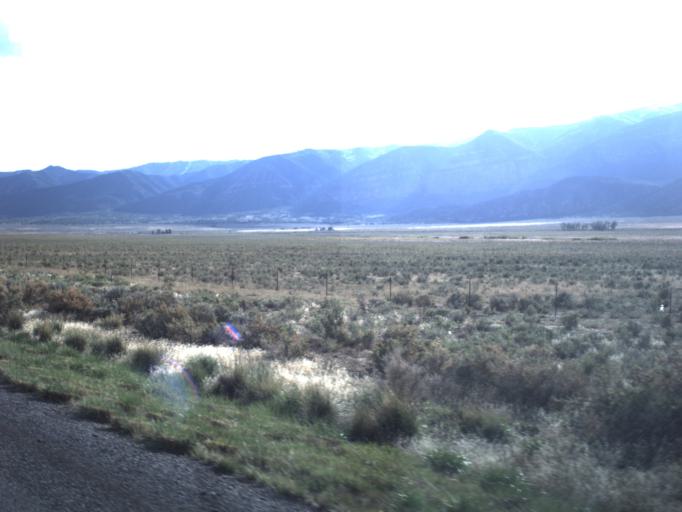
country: US
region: Utah
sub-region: Sevier County
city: Aurora
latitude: 39.0654
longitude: -112.0421
